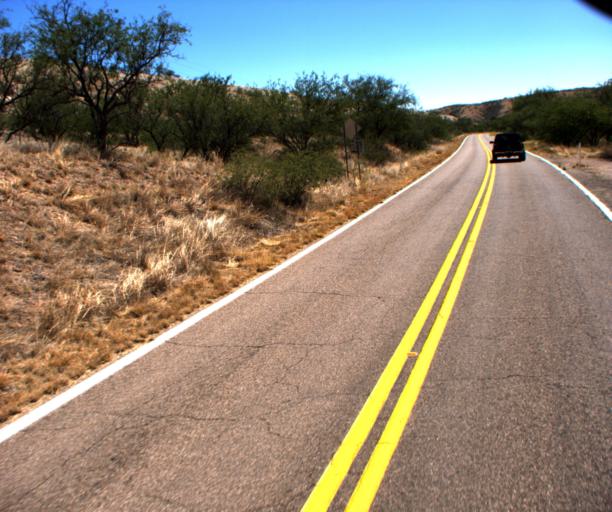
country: US
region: Arizona
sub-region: Santa Cruz County
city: Rio Rico
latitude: 31.3951
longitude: -111.0422
